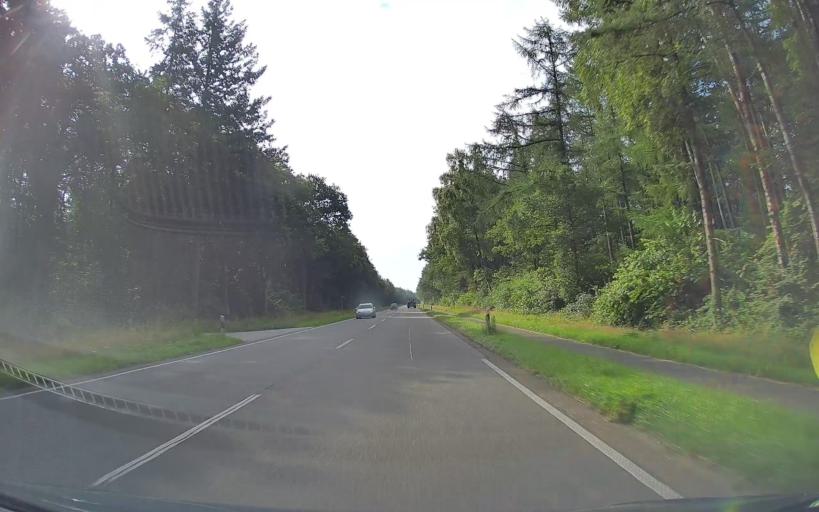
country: DE
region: Lower Saxony
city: Bosel
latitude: 52.9719
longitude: 7.9128
